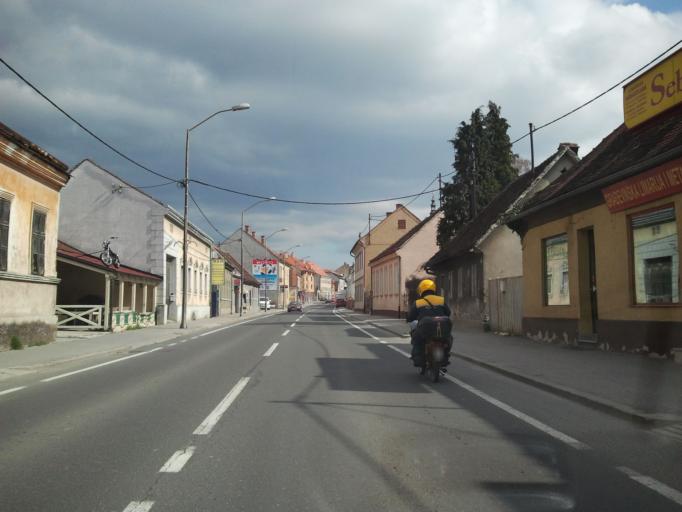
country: HR
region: Zagrebacka
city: Jastrebarsko
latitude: 45.6698
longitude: 15.6489
